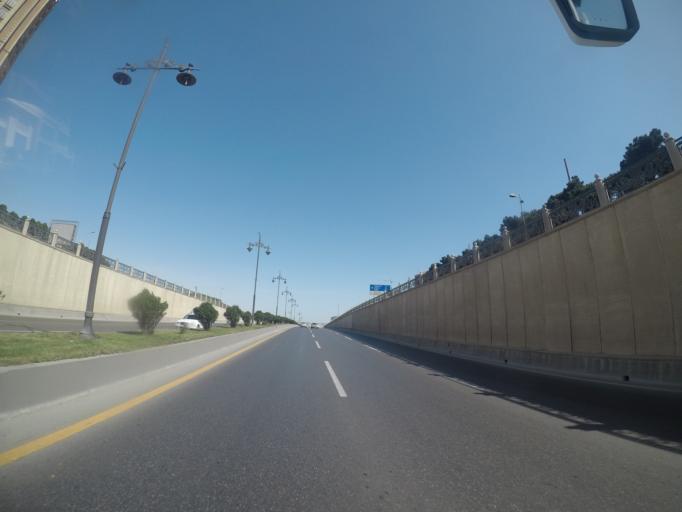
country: AZ
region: Baki
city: Bilajari
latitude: 40.4138
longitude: 49.8019
